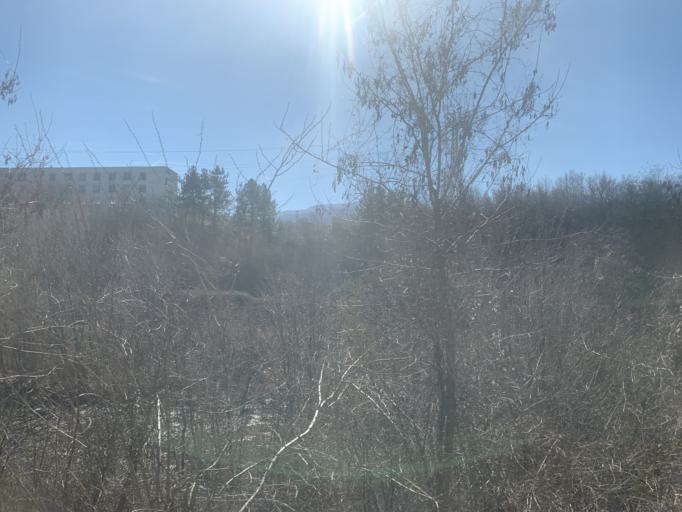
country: BG
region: Pazardzhik
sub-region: Obshtina Belovo
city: Belovo
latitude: 42.2103
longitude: 24.0321
